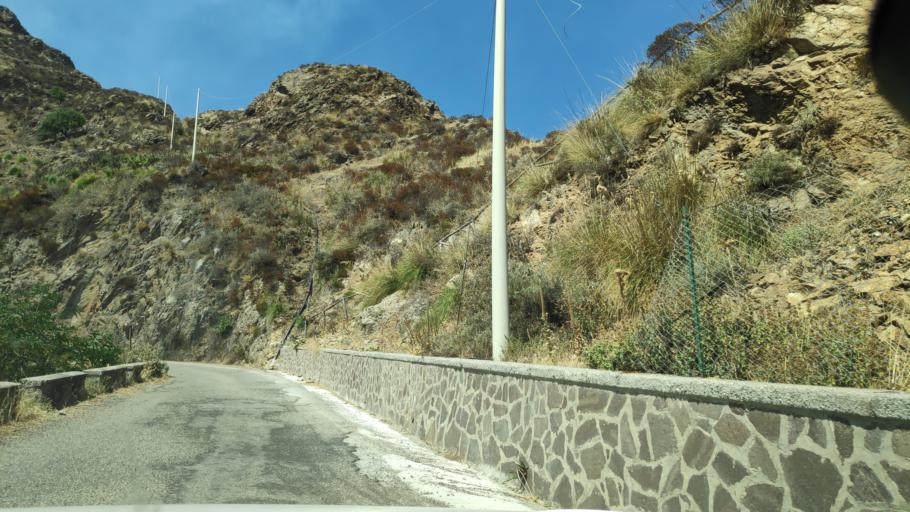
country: IT
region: Calabria
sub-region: Provincia di Reggio Calabria
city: Bova
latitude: 37.9993
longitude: 15.9304
